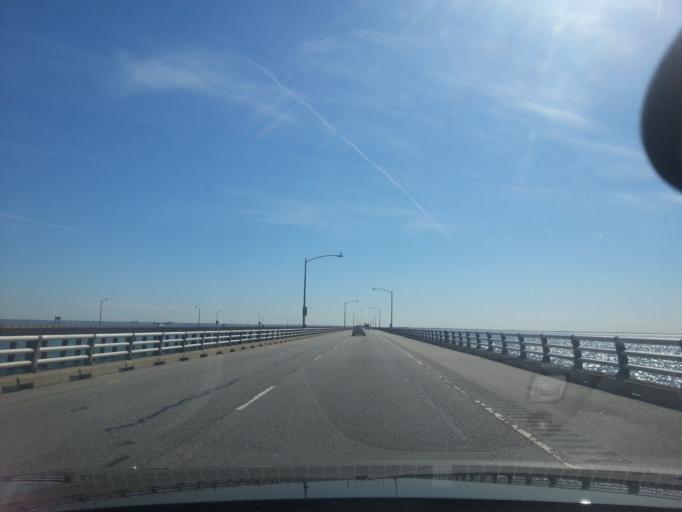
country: US
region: Virginia
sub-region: City of Virginia Beach
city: Virginia Beach
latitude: 37.0234
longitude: -76.0900
